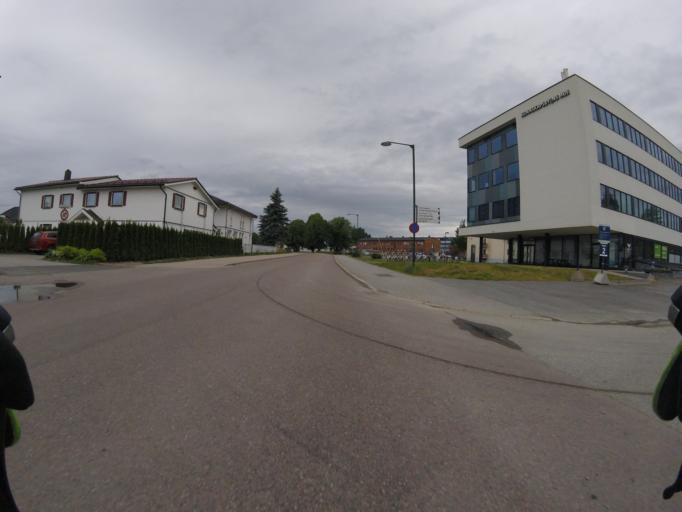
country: NO
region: Akershus
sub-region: Skedsmo
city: Lillestrom
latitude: 59.9738
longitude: 11.0477
